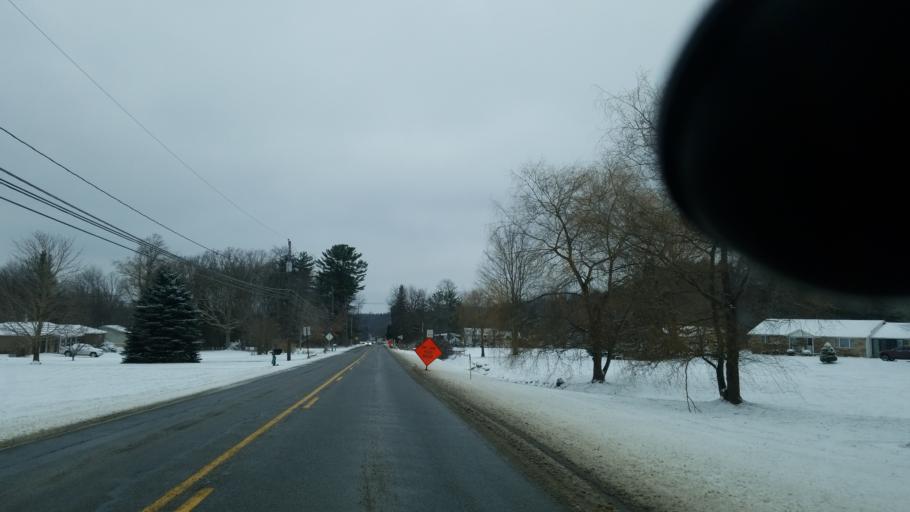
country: US
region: Pennsylvania
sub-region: Indiana County
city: Johnsonburg
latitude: 40.9263
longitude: -78.8939
